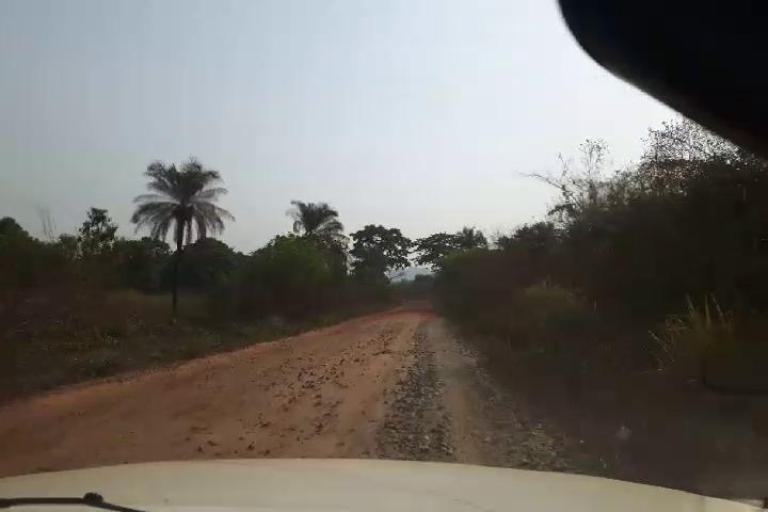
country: SL
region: Northern Province
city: Masingbi
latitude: 8.8481
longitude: -11.8293
